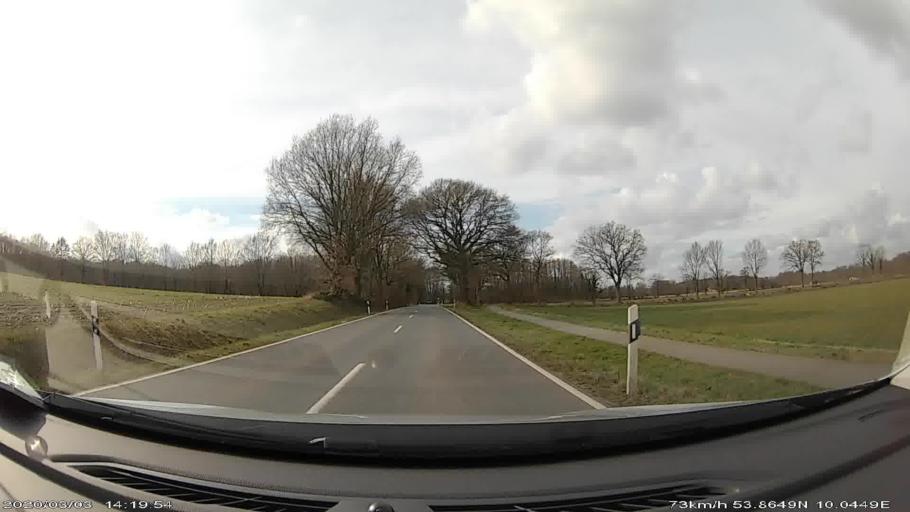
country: DE
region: Schleswig-Holstein
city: Struvenhutten
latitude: 53.8650
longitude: 10.0443
